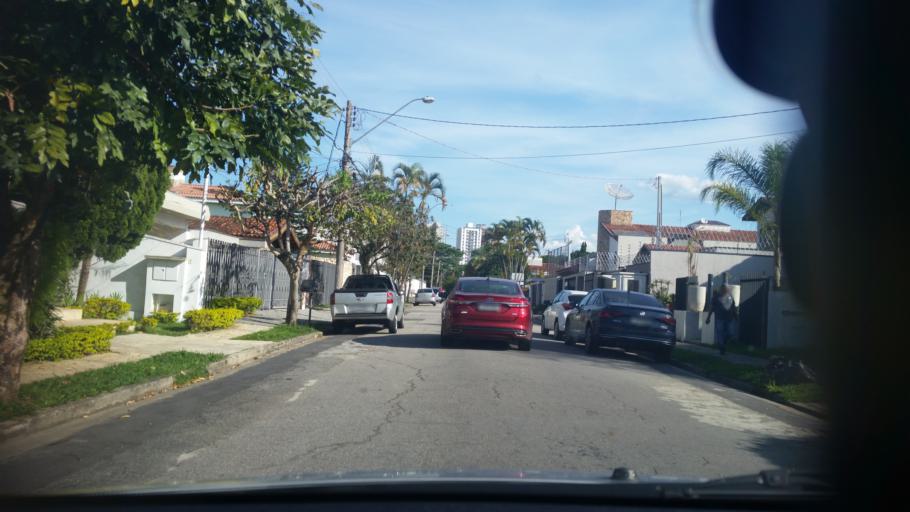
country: BR
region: Sao Paulo
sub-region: Taubate
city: Taubate
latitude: -23.0295
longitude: -45.5727
